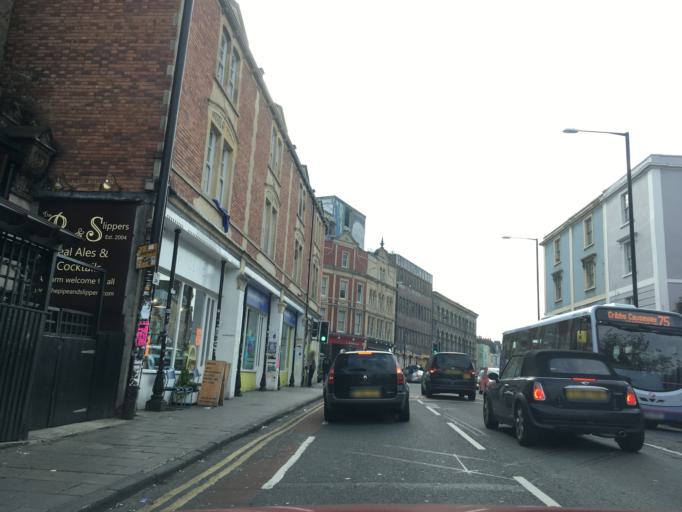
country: GB
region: England
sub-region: Bristol
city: Bristol
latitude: 51.4647
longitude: -2.5899
